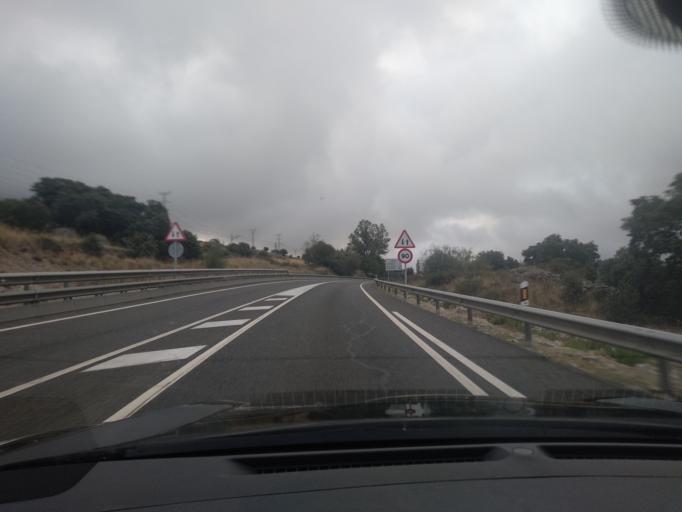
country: ES
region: Castille and Leon
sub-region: Provincia de Segovia
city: Otero de Herreros
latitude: 40.7883
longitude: -4.2136
